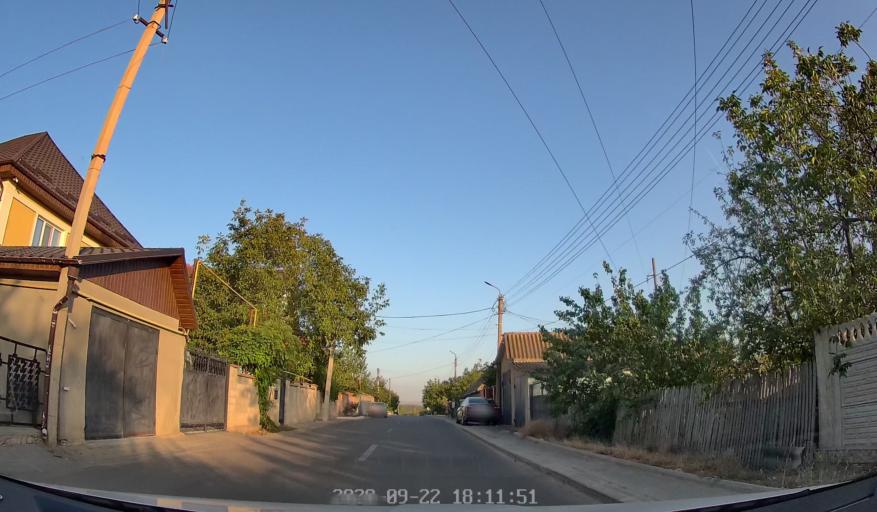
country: MD
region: Laloveni
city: Ialoveni
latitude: 46.9489
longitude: 28.7850
